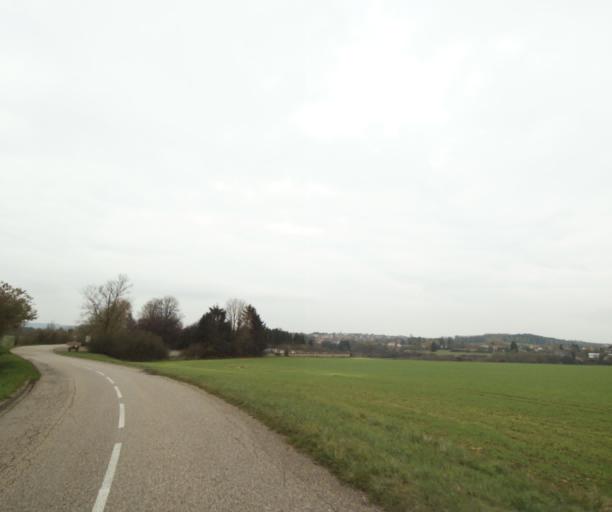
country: FR
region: Lorraine
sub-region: Departement de Meurthe-et-Moselle
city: Mancieulles
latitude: 49.2758
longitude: 5.8908
